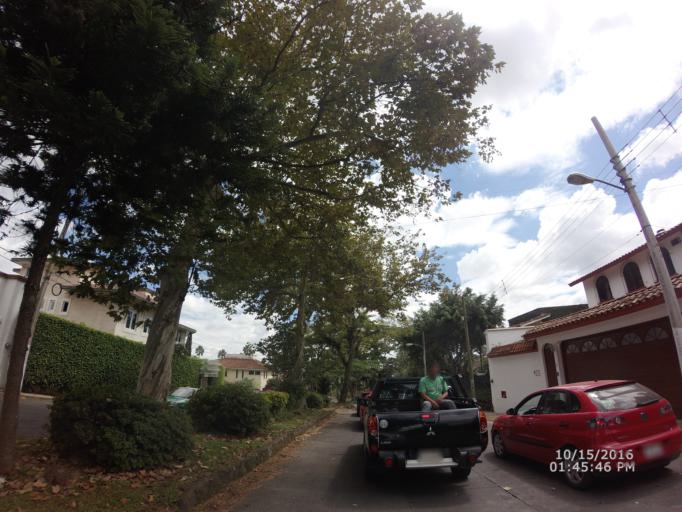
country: MX
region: Veracruz
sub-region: Xalapa
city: Lomas Verdes
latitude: 19.5256
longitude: -96.8842
